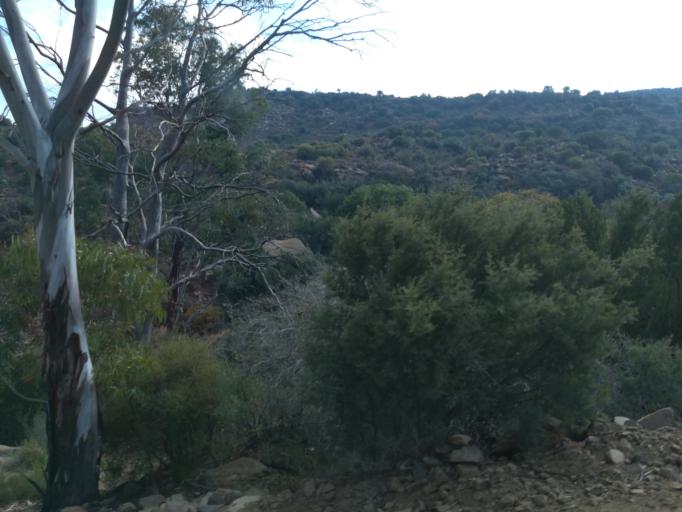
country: LS
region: Quthing
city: Quthing
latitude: -30.3374
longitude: 27.5456
